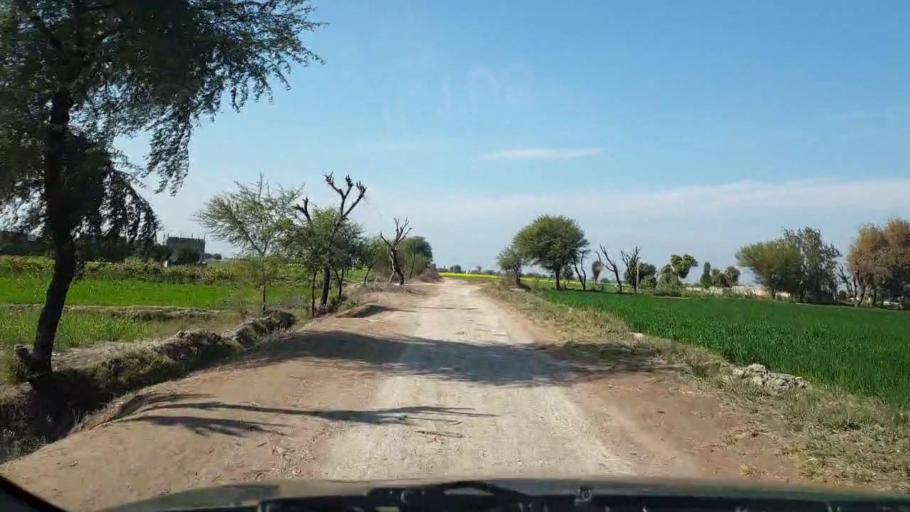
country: PK
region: Sindh
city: Sinjhoro
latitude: 25.9777
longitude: 68.7918
